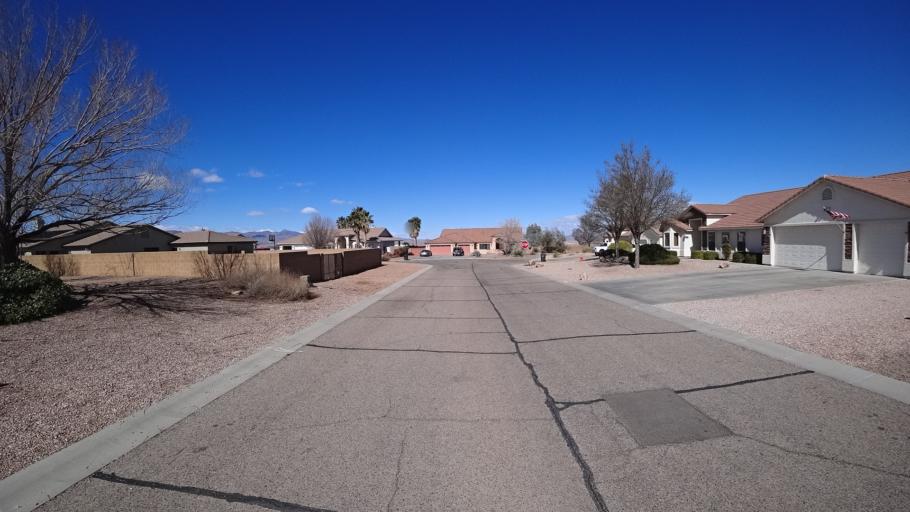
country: US
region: Arizona
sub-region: Mohave County
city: New Kingman-Butler
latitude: 35.2094
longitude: -113.9713
